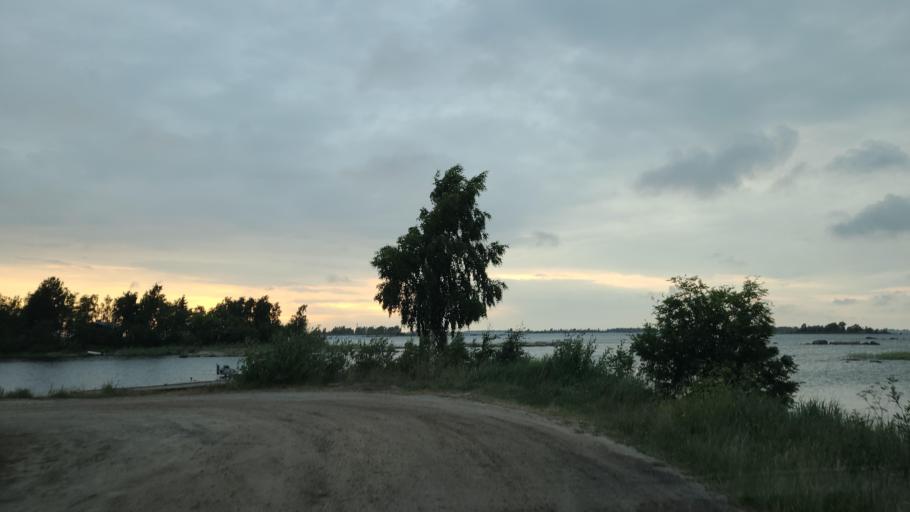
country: FI
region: Ostrobothnia
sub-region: Vaasa
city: Replot
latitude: 63.3235
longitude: 21.1394
